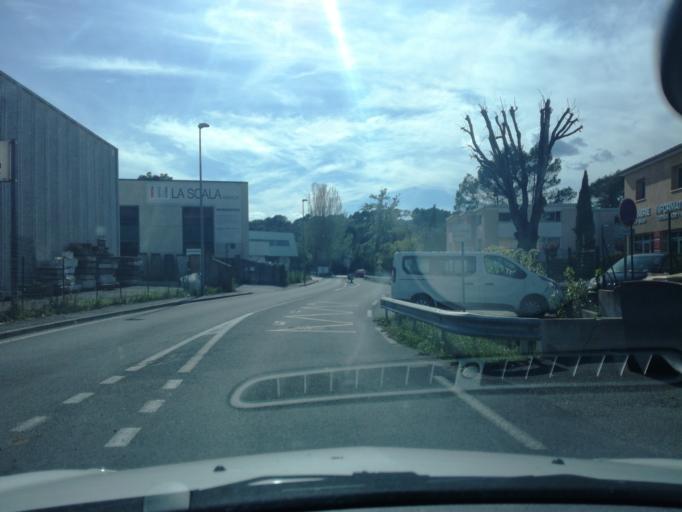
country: FR
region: Provence-Alpes-Cote d'Azur
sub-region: Departement des Alpes-Maritimes
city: Mouans-Sartoux
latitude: 43.6143
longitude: 6.9654
